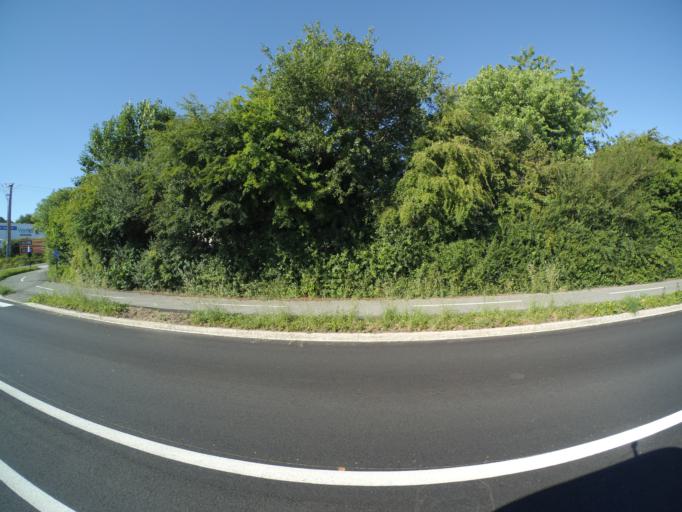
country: FR
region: Pays de la Loire
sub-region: Departement de la Vendee
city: Les Herbiers
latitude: 46.8758
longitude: -1.0264
